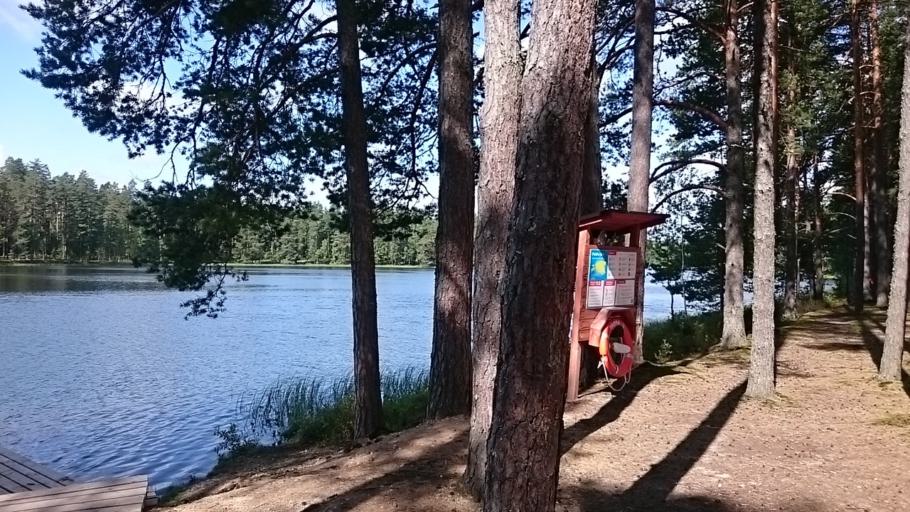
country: EE
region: Vorumaa
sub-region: Voru linn
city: Voru
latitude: 57.9105
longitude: 27.1916
